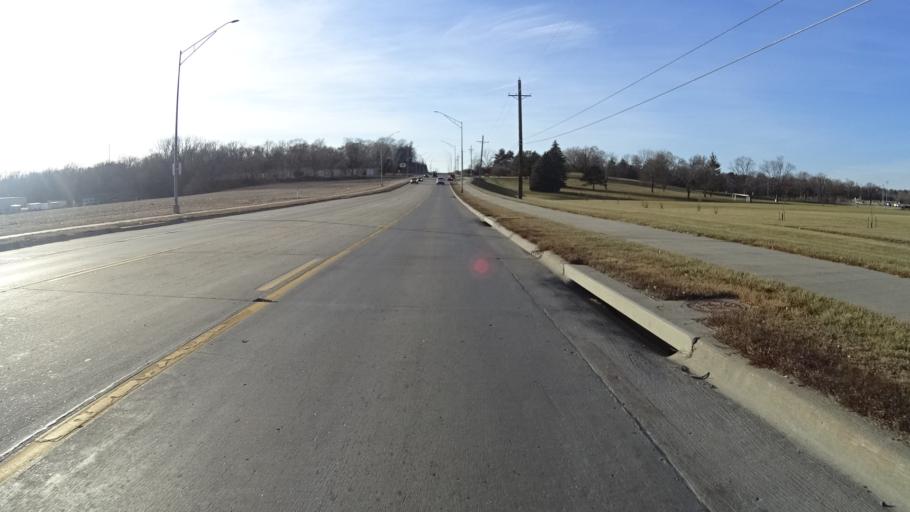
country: US
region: Nebraska
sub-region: Sarpy County
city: La Vista
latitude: 41.1908
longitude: -96.0144
